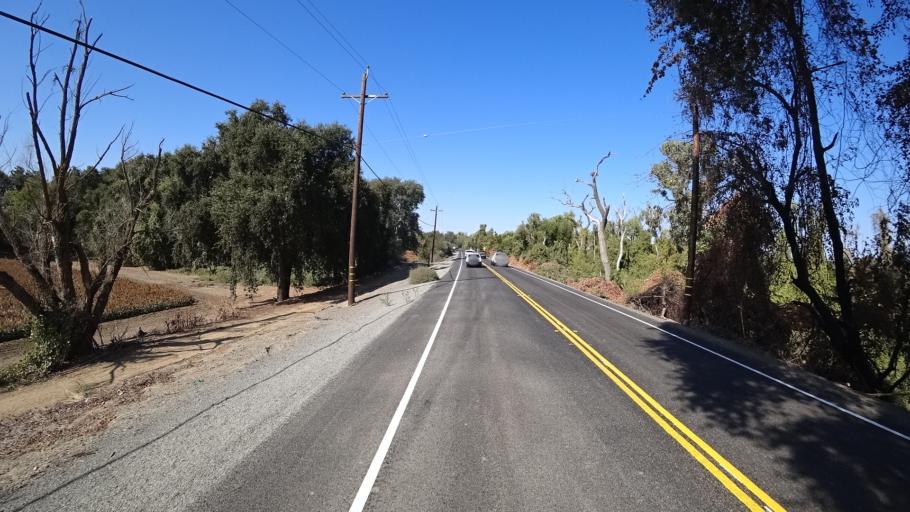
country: US
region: California
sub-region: Yolo County
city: West Sacramento
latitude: 38.6576
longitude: -121.6086
